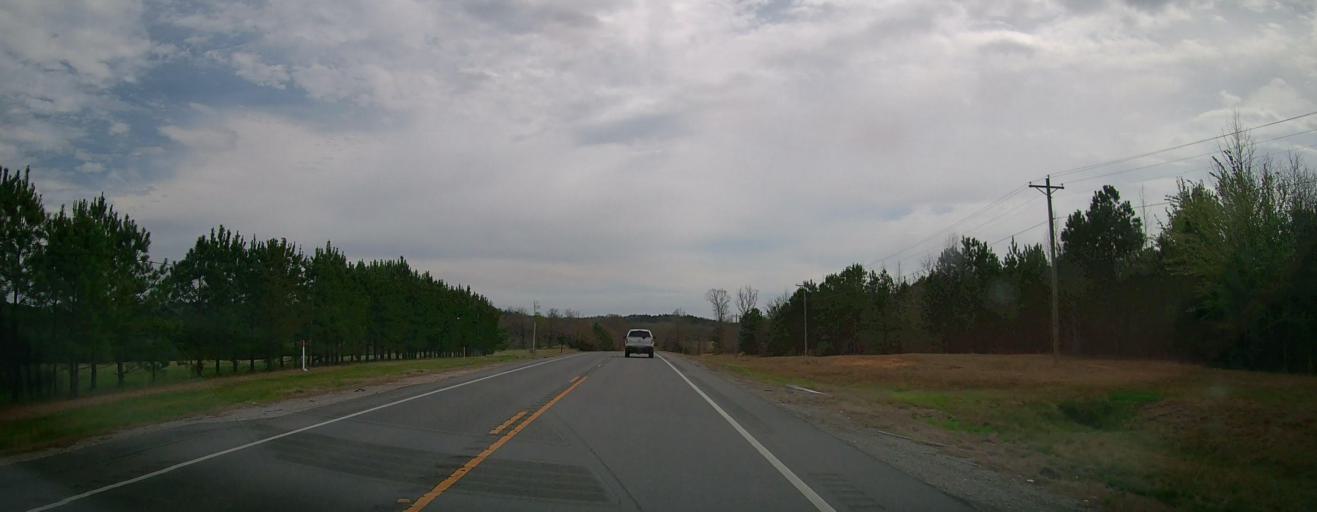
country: US
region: Alabama
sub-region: Marion County
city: Guin
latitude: 34.0065
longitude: -87.9336
